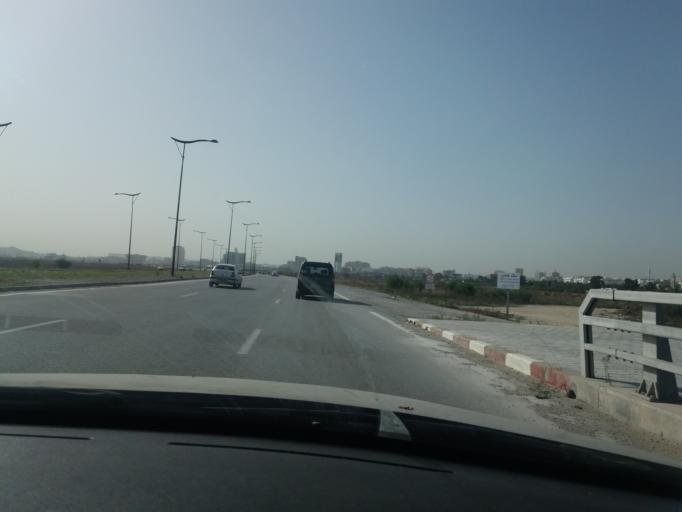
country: TN
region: Tunis
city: Tunis
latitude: 36.8200
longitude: 10.1990
